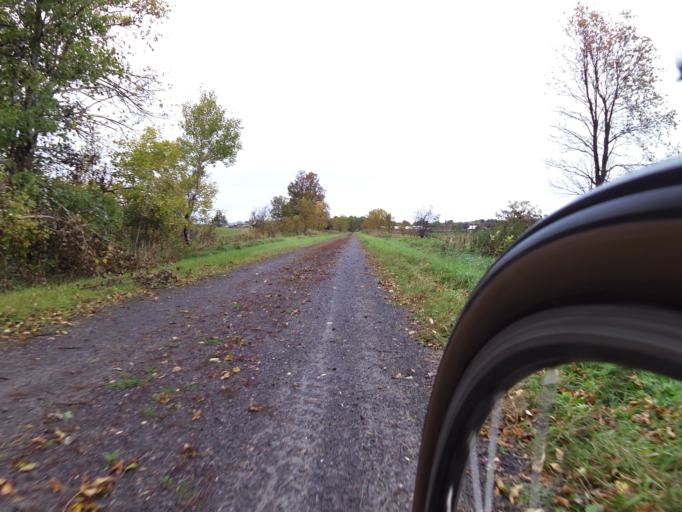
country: CA
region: Quebec
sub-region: Outaouais
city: Shawville
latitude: 45.7096
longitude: -76.5888
